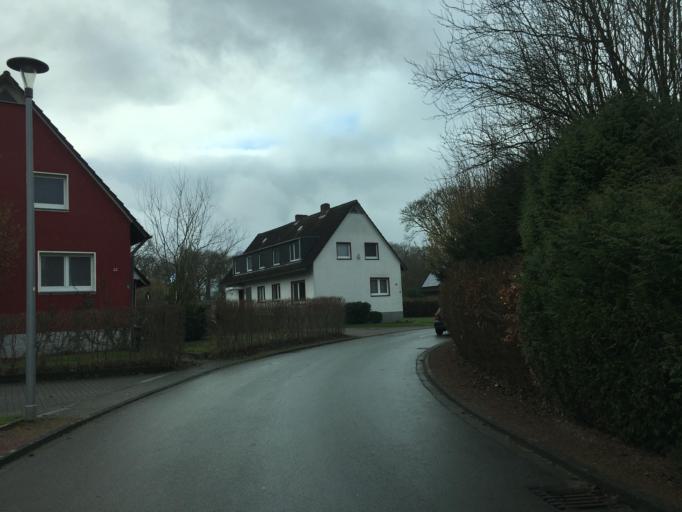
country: DE
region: North Rhine-Westphalia
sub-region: Regierungsbezirk Munster
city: Muenster
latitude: 51.9268
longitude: 7.5662
